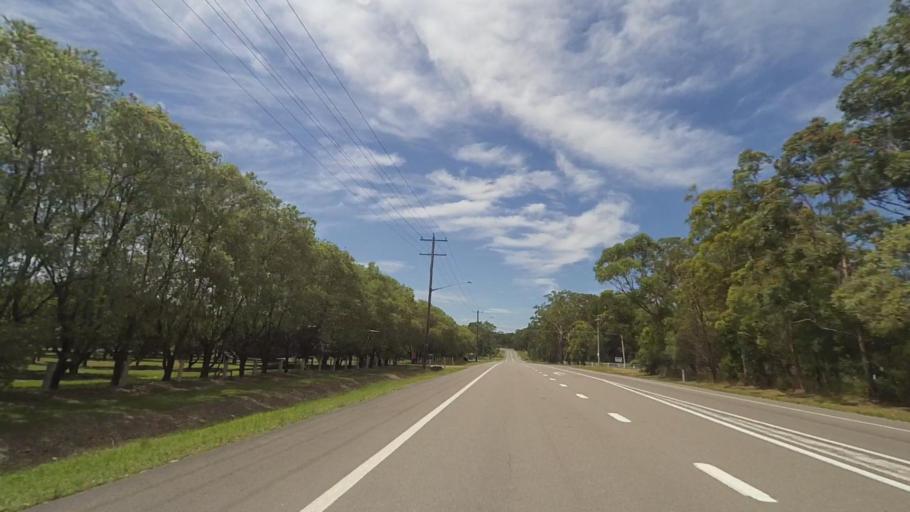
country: AU
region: New South Wales
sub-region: Port Stephens Shire
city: Medowie
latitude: -32.7537
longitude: 151.8680
